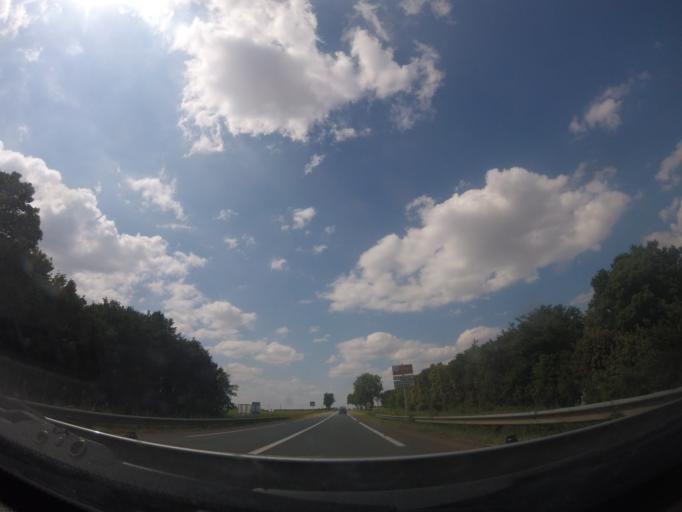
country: FR
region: Poitou-Charentes
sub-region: Departement de la Charente-Maritime
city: Saint-Porchaire
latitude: 45.8326
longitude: -0.8008
